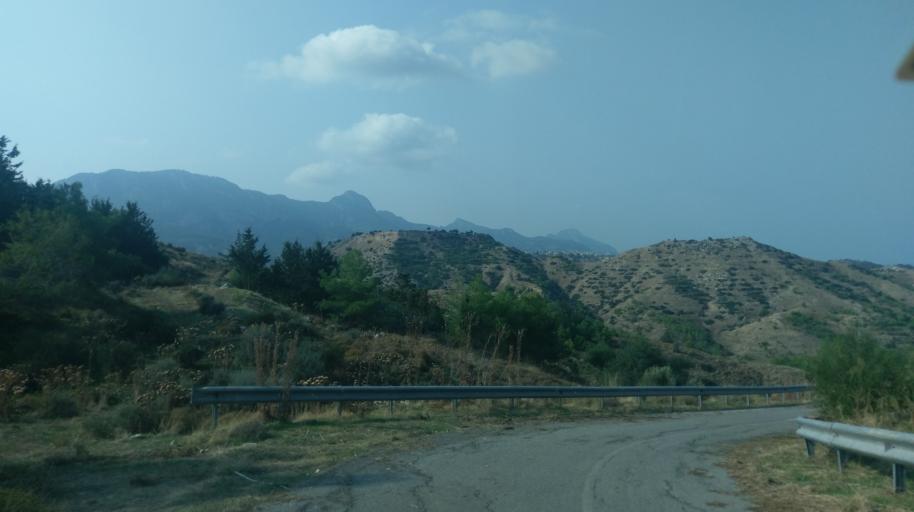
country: CY
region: Keryneia
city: Kyrenia
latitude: 35.3118
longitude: 33.4685
